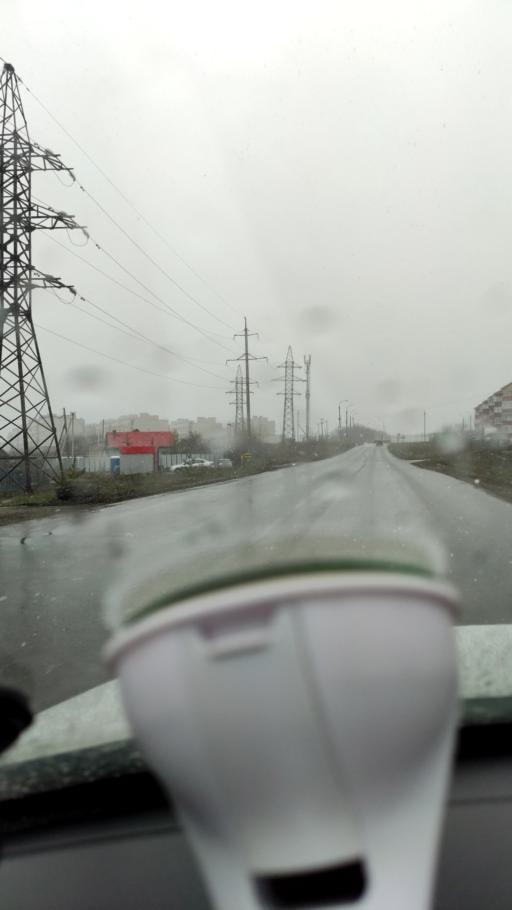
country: RU
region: Samara
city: Novosemeykino
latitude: 53.3304
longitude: 50.3143
